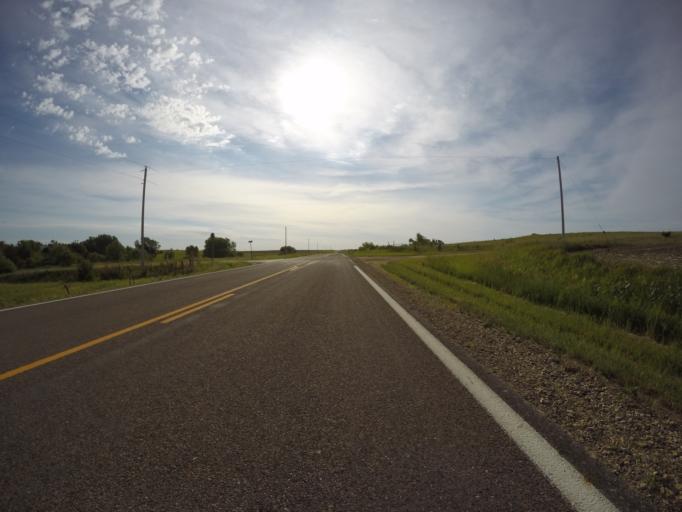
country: US
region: Kansas
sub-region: Republic County
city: Belleville
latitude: 39.7120
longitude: -97.3879
